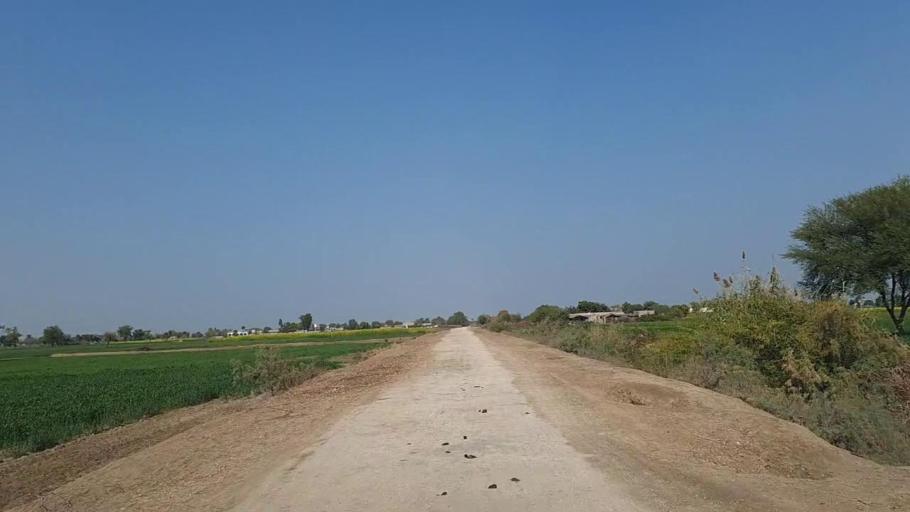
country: PK
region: Sindh
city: Nawabshah
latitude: 26.2758
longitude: 68.5135
